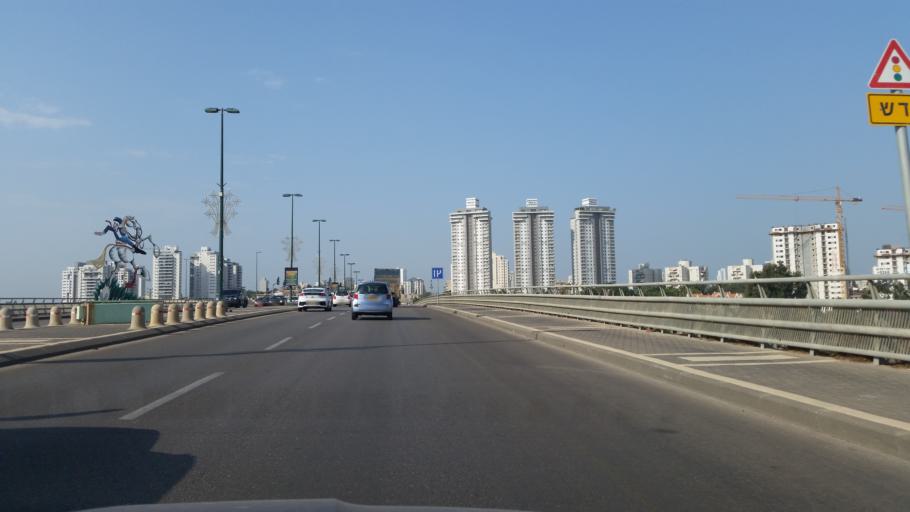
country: IL
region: Central District
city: Netanya
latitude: 32.3122
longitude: 34.8680
